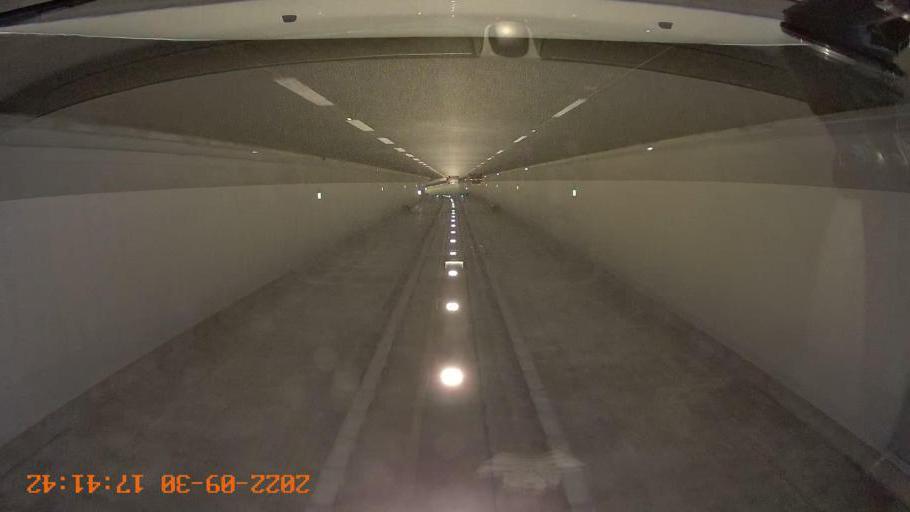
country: PL
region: Lesser Poland Voivodeship
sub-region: Krakow
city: Krakow
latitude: 50.0218
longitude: 19.9299
